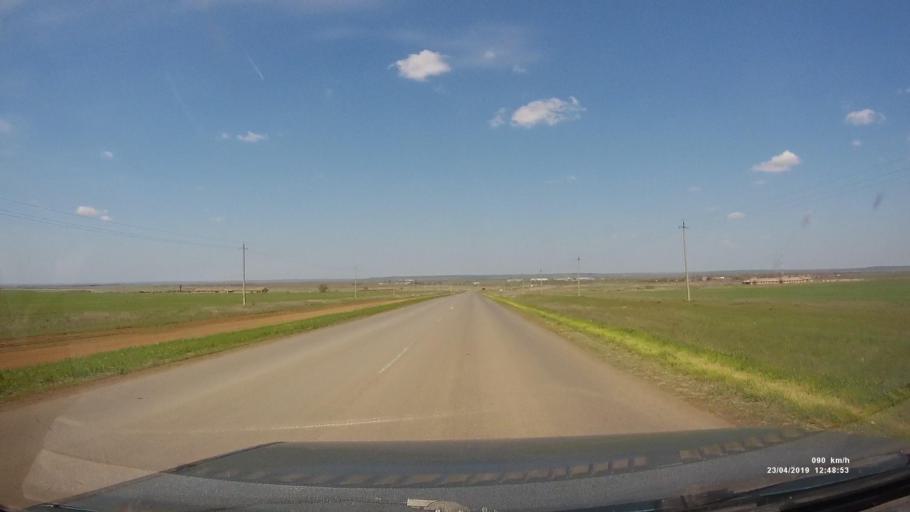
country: RU
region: Kalmykiya
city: Yashalta
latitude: 46.5301
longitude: 42.6389
